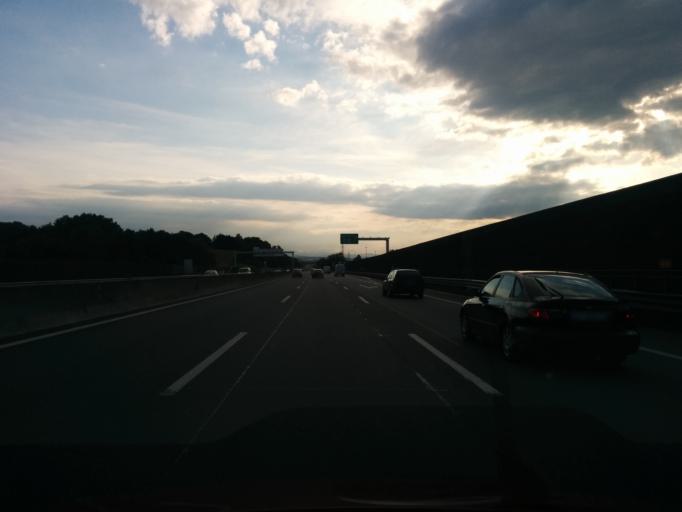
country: AT
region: Lower Austria
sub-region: Politischer Bezirk Melk
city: Ybbs an der Donau
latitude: 48.1570
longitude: 15.1057
